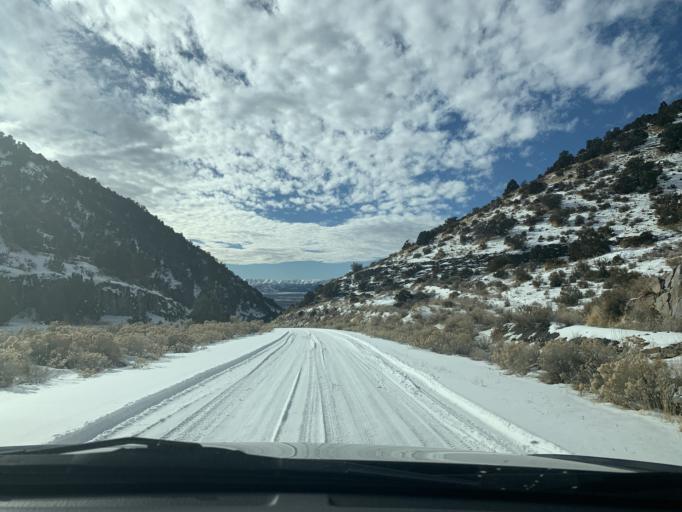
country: US
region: Utah
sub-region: Tooele County
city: Tooele
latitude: 40.3137
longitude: -112.2385
